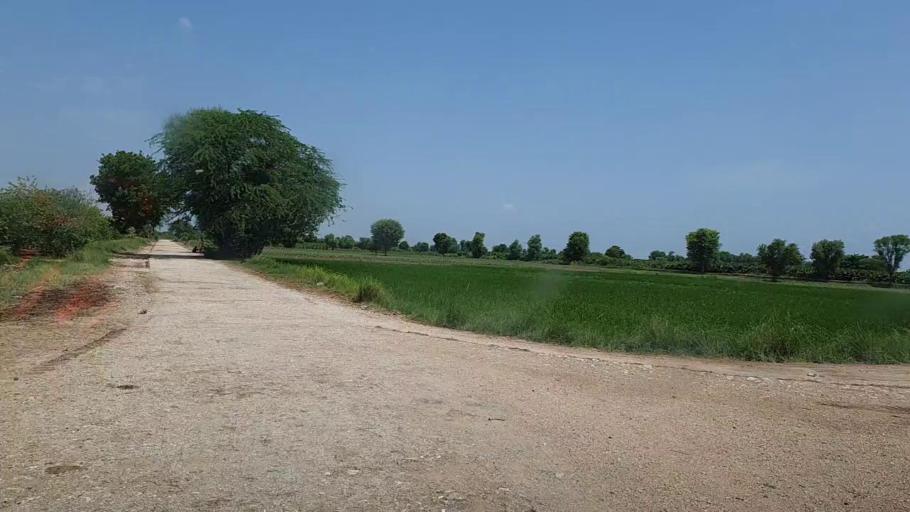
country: PK
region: Sindh
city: Bhiria
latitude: 26.8909
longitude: 68.1987
